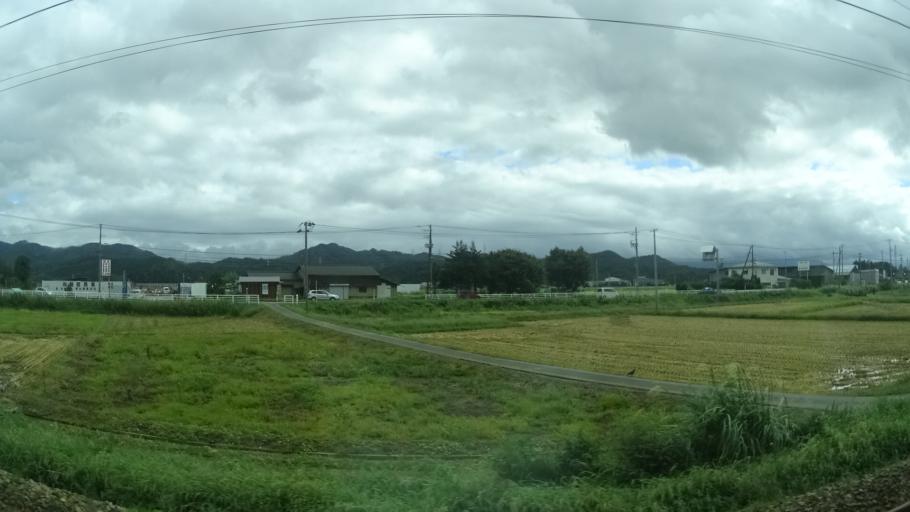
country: JP
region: Niigata
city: Shibata
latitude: 37.9796
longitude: 139.3599
